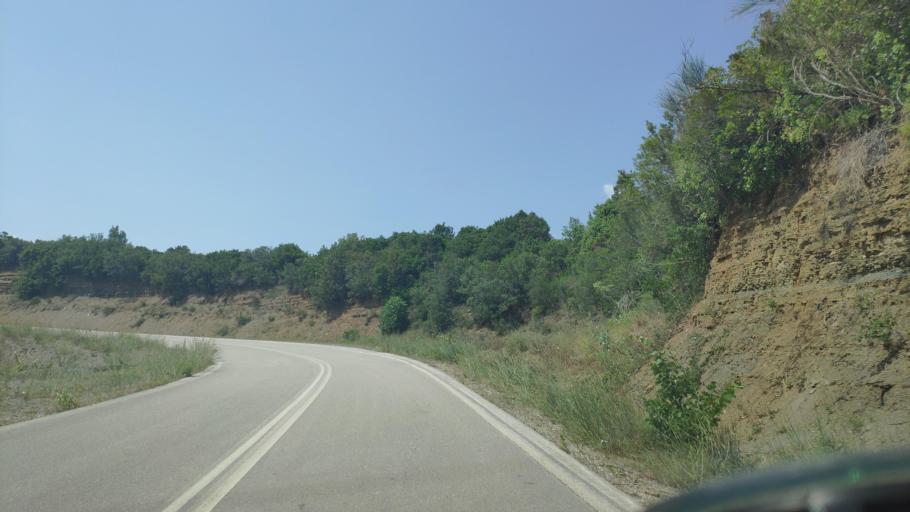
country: GR
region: Epirus
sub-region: Nomos Artas
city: Ano Kalentini
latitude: 39.2198
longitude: 21.1437
